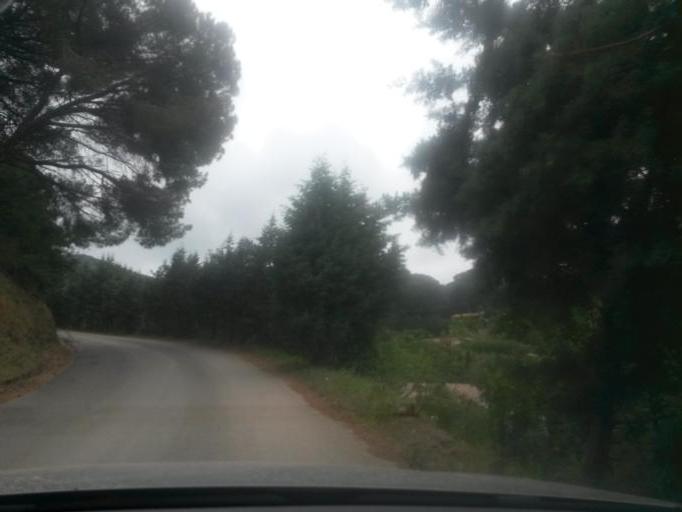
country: IT
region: Tuscany
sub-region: Provincia di Livorno
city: Porto Azzurro
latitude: 42.7466
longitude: 10.4022
